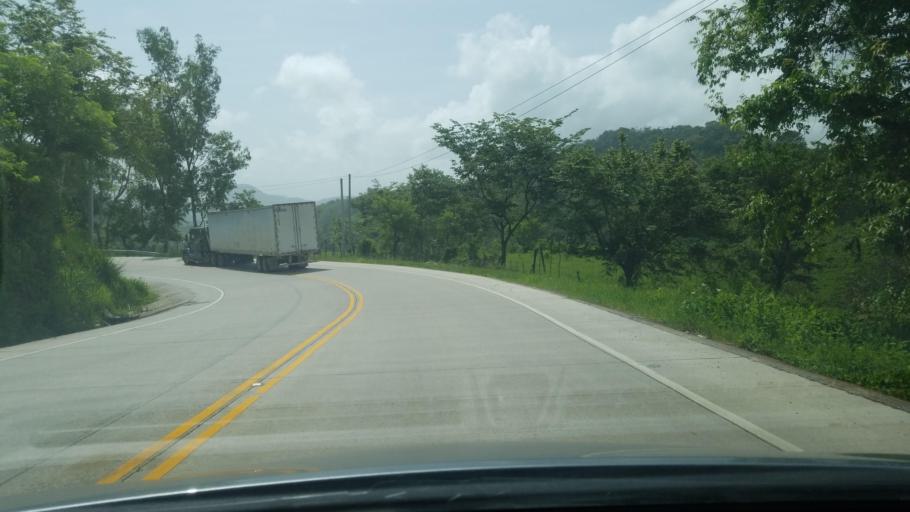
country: HN
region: Copan
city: San Jeronimo
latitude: 14.9604
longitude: -88.8943
